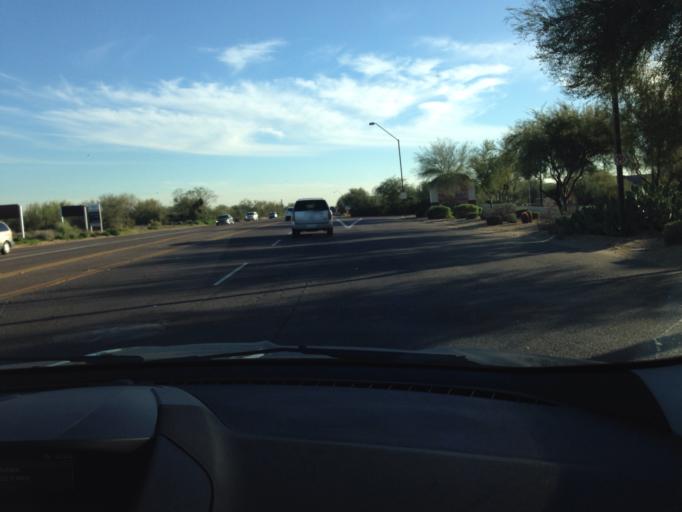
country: US
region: Arizona
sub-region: Maricopa County
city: Cave Creek
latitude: 33.7410
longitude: -111.9783
